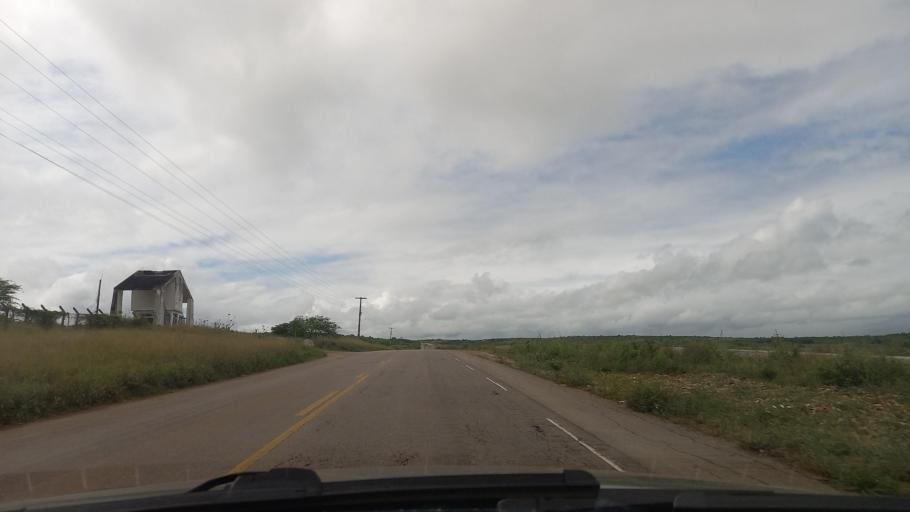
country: BR
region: Alagoas
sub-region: Batalha
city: Batalha
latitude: -9.6539
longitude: -37.1798
